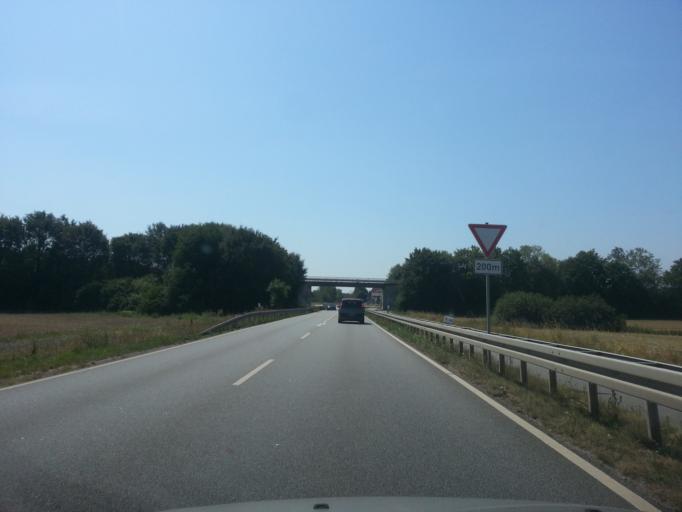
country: DE
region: Hesse
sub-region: Regierungsbezirk Darmstadt
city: Biblis
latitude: 49.6976
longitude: 8.4671
